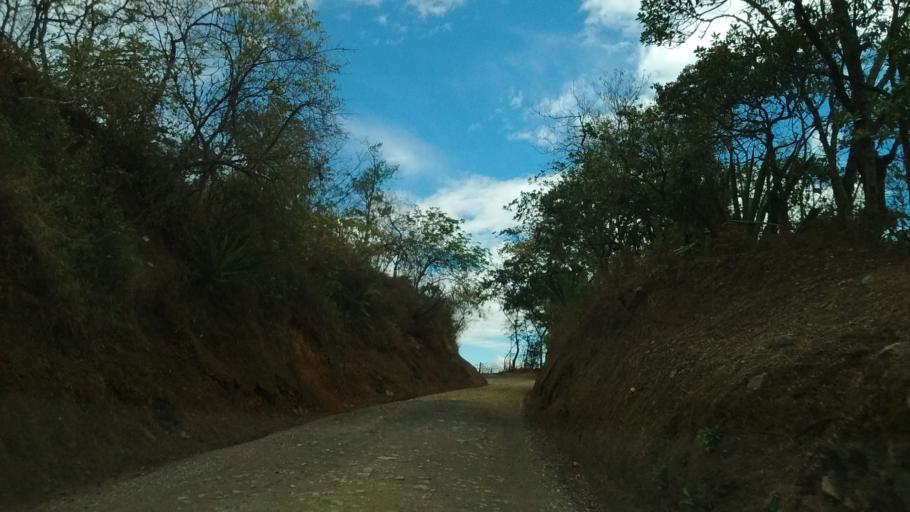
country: CO
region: Cauca
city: Almaguer
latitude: 1.8436
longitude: -76.9113
